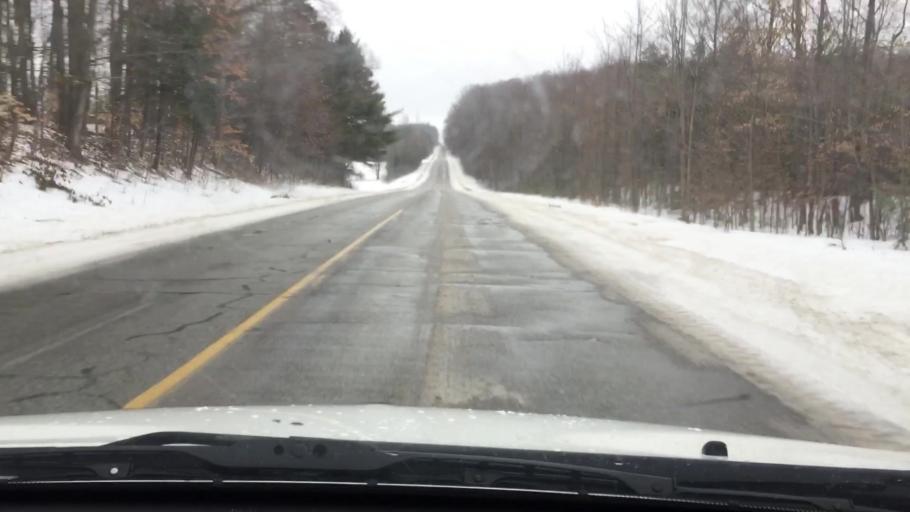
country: US
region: Michigan
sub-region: Wexford County
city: Cadillac
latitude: 44.1931
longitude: -85.4057
